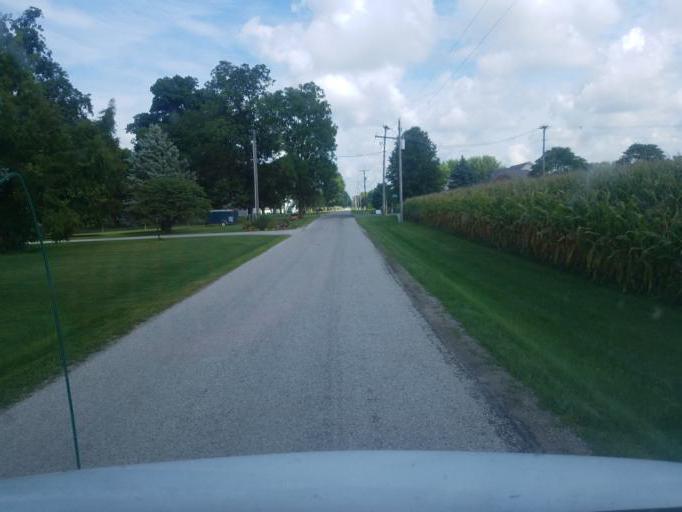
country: US
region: Ohio
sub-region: Marion County
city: Marion
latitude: 40.5103
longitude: -83.0838
